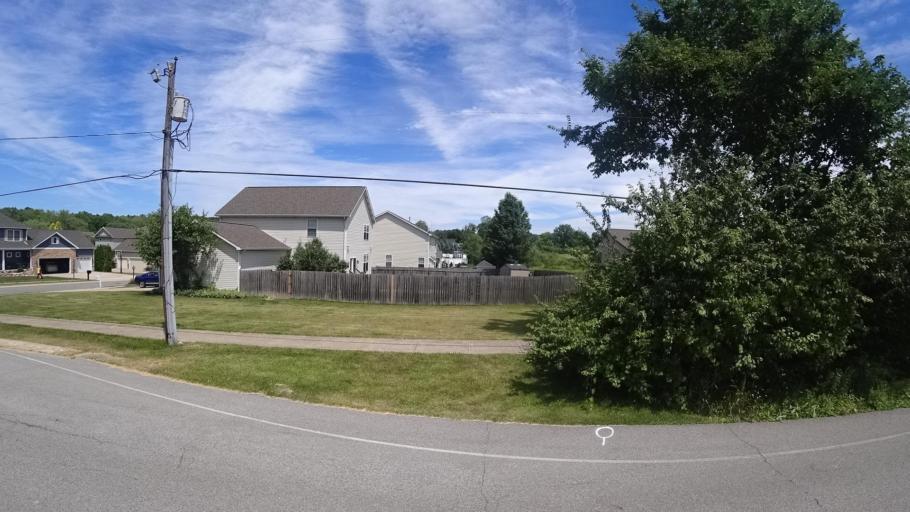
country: US
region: Indiana
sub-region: Porter County
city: Porter
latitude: 41.6331
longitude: -87.0770
